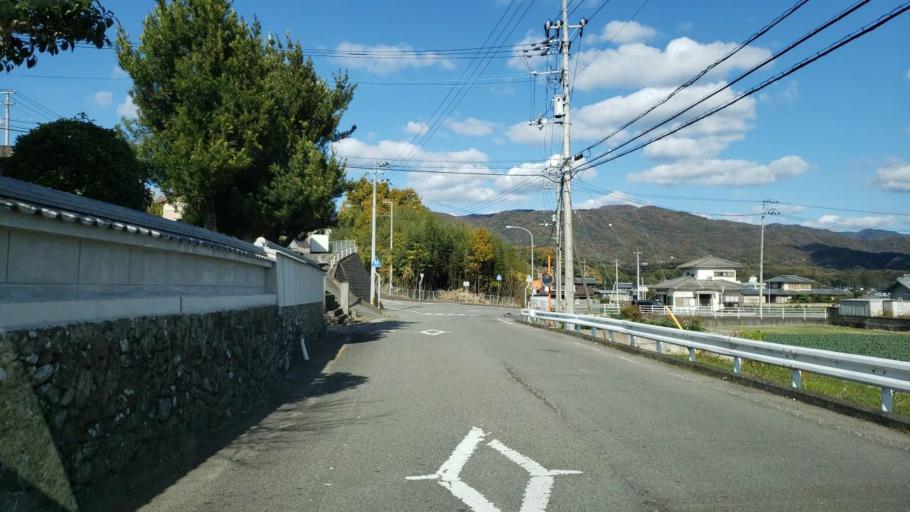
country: JP
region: Tokushima
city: Wakimachi
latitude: 34.0692
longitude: 134.1913
